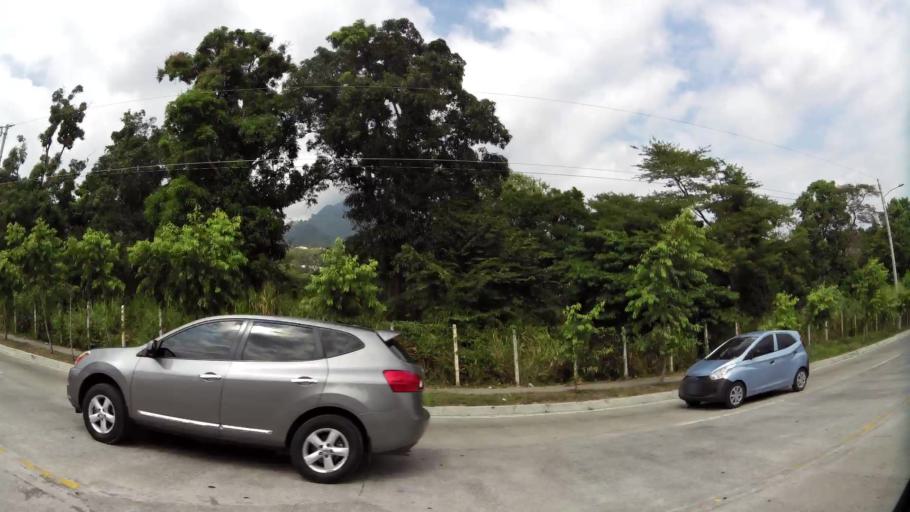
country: SV
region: San Salvador
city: Mejicanos
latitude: 13.7142
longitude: -89.2455
